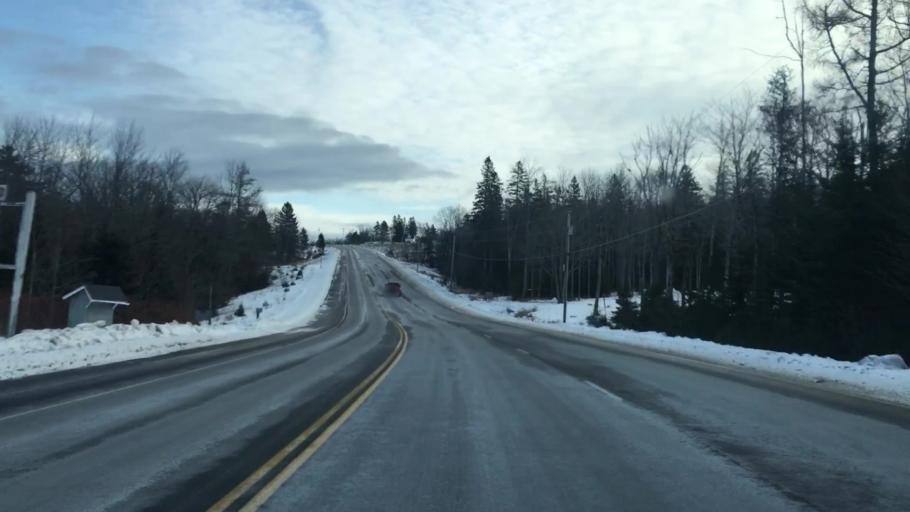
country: US
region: Maine
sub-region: Washington County
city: Machias
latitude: 44.9503
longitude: -67.6702
